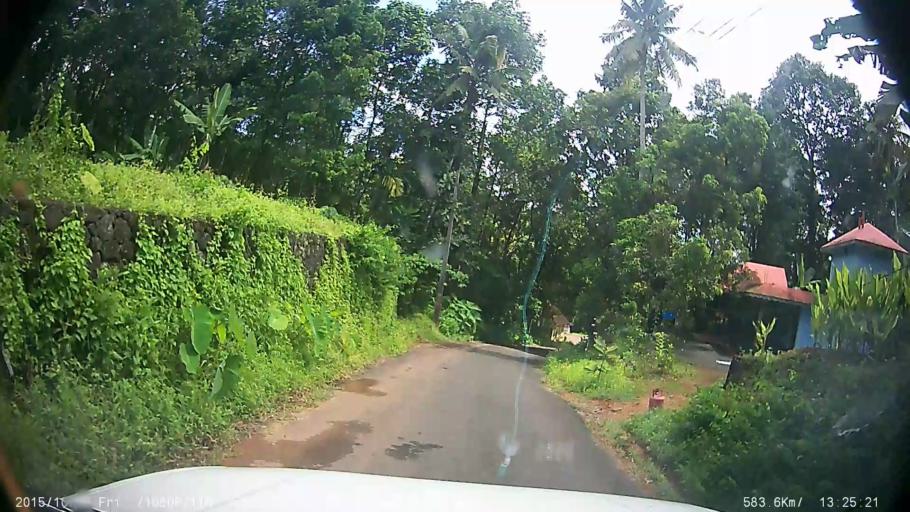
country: IN
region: Kerala
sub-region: Ernakulam
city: Muvattupuzha
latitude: 9.9226
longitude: 76.5674
